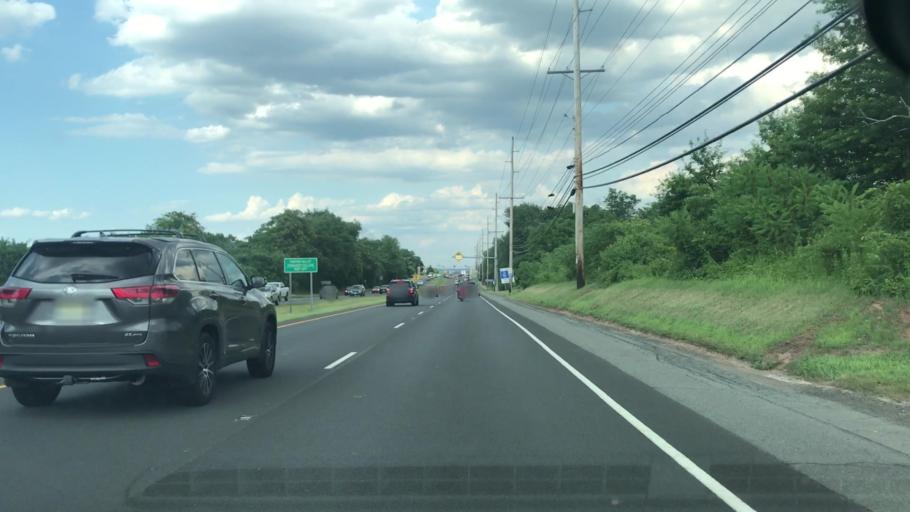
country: US
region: New Jersey
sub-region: Somerset County
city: Bradley Gardens
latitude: 40.5593
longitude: -74.7068
